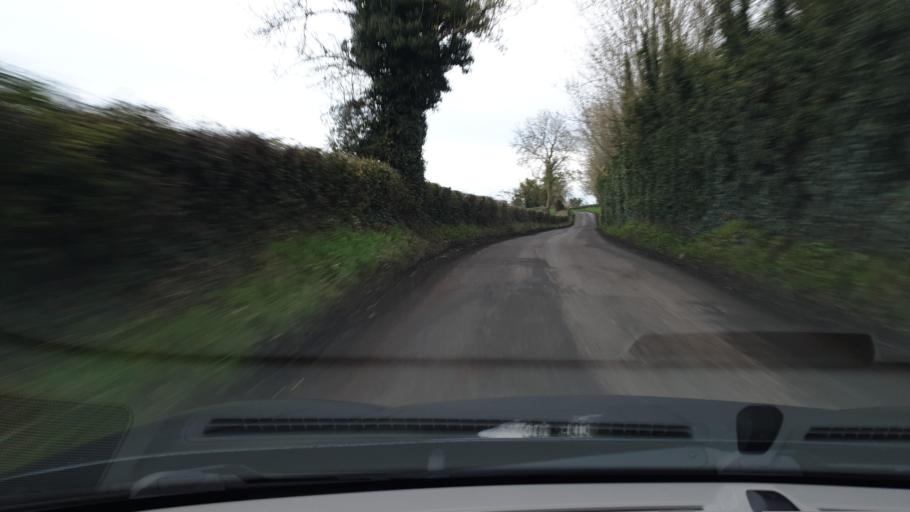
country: IE
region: Leinster
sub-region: An Mhi
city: Ashbourne
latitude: 53.5390
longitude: -6.3384
